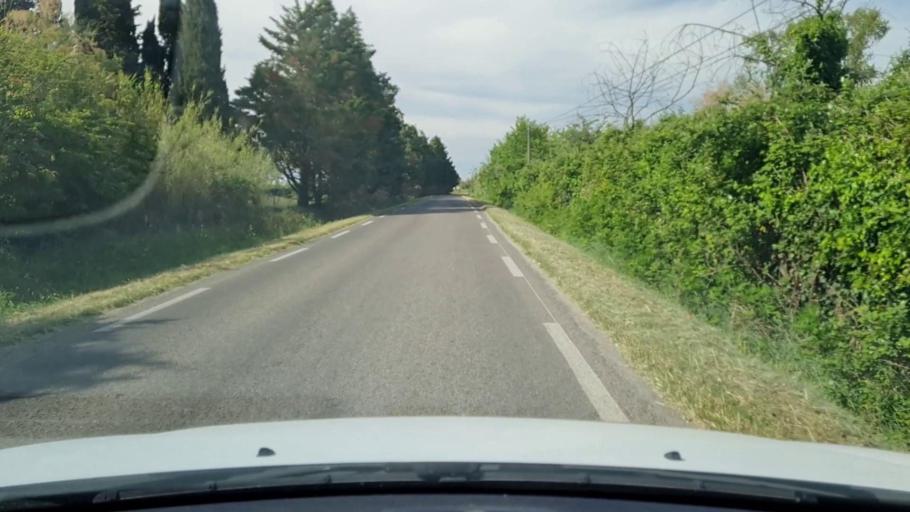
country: FR
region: Languedoc-Roussillon
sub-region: Departement du Gard
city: Aigues-Mortes
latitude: 43.6046
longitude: 4.2135
